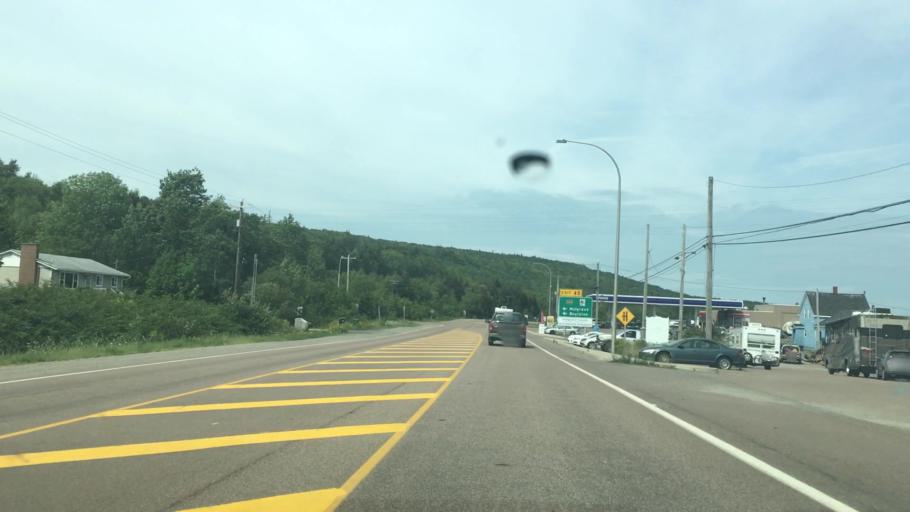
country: CA
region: Nova Scotia
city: Port Hawkesbury
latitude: 45.6480
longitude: -61.4375
